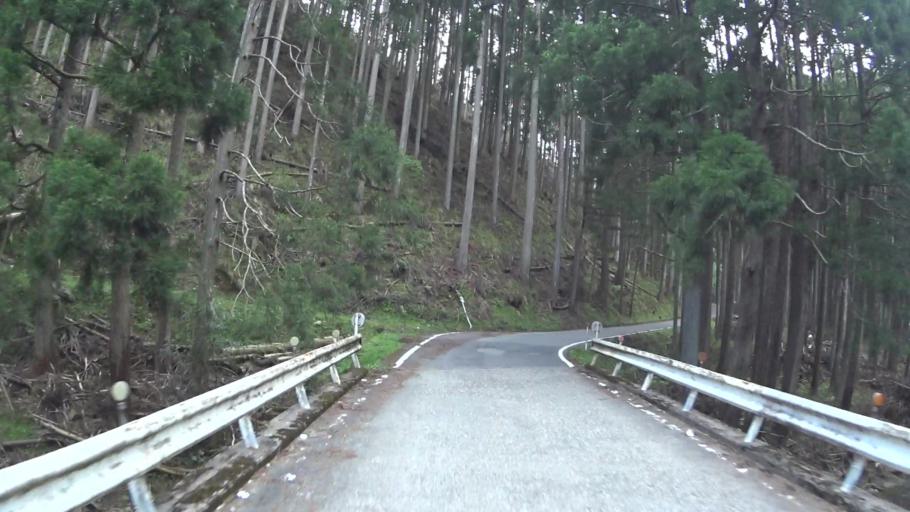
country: JP
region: Kyoto
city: Kameoka
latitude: 35.1231
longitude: 135.5926
